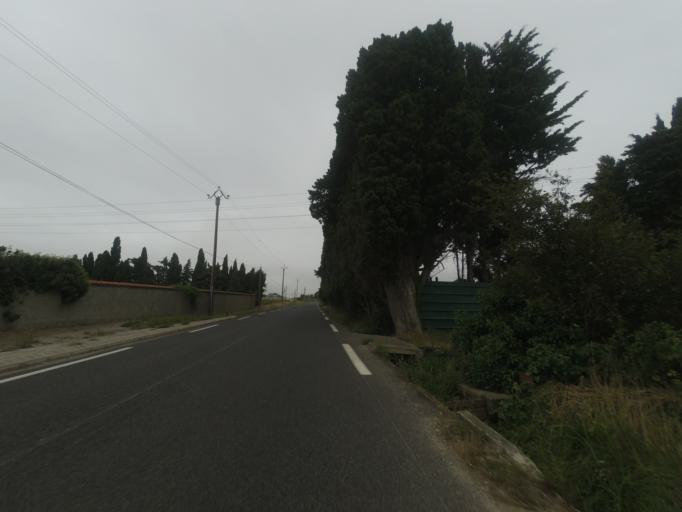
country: FR
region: Languedoc-Roussillon
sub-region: Departement des Pyrenees-Orientales
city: Pezilla-la-Riviere
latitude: 42.6932
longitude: 2.7849
